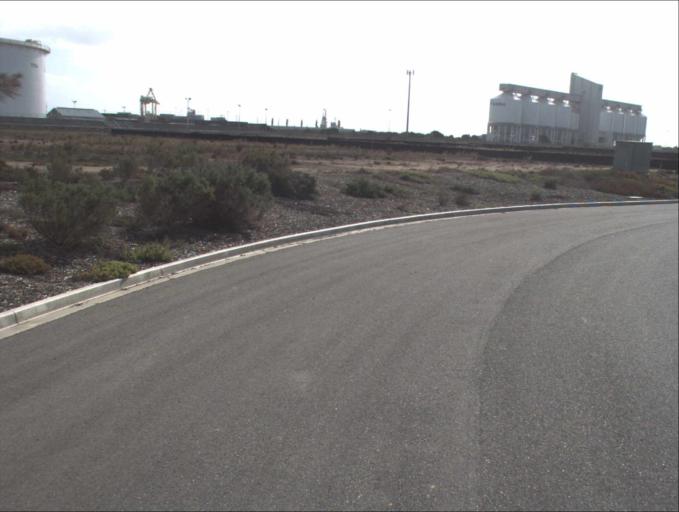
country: AU
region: South Australia
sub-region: Port Adelaide Enfield
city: Birkenhead
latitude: -34.7764
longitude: 138.5060
